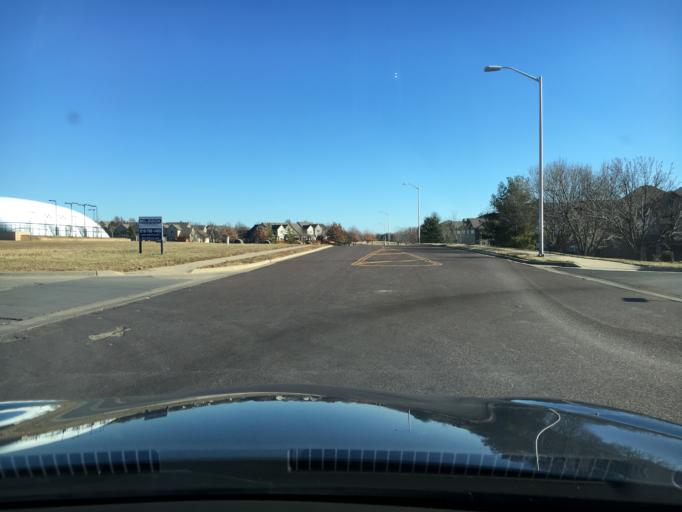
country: US
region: Kansas
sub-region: Johnson County
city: Lenexa
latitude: 38.8654
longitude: -94.6666
